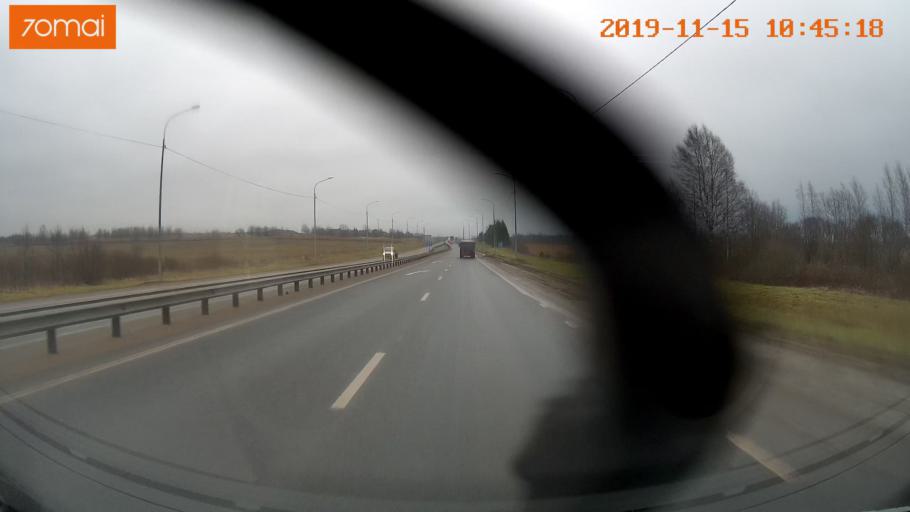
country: RU
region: Vologda
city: Sheksna
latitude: 59.2107
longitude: 38.5839
